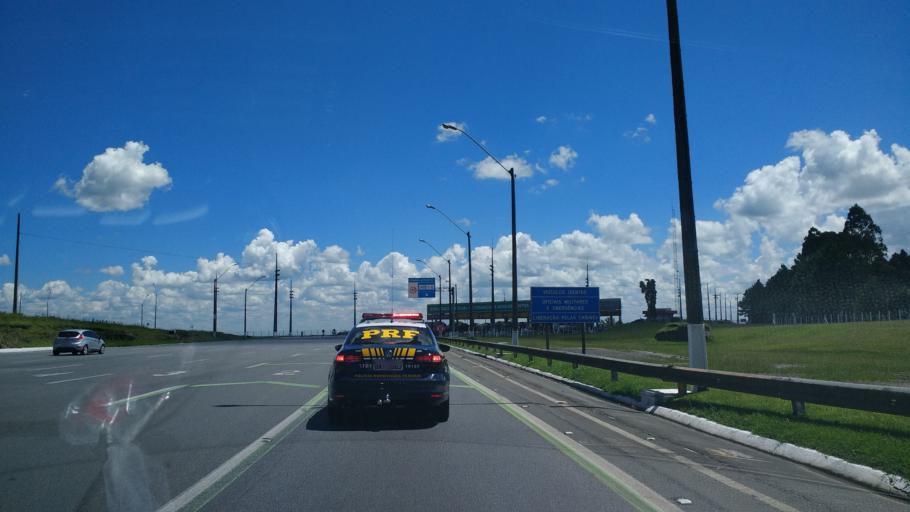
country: BR
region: Parana
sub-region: Campo Largo
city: Campo Largo
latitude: -25.4701
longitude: -49.6598
